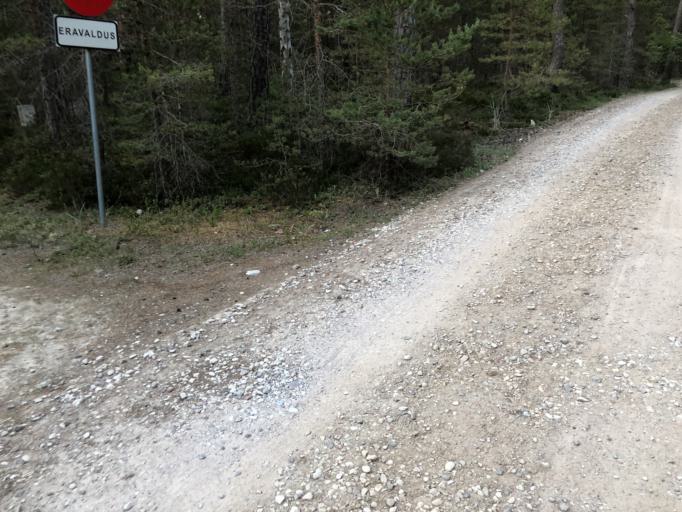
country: EE
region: Harju
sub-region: Paldiski linn
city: Paldiski
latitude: 59.3912
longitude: 24.2226
